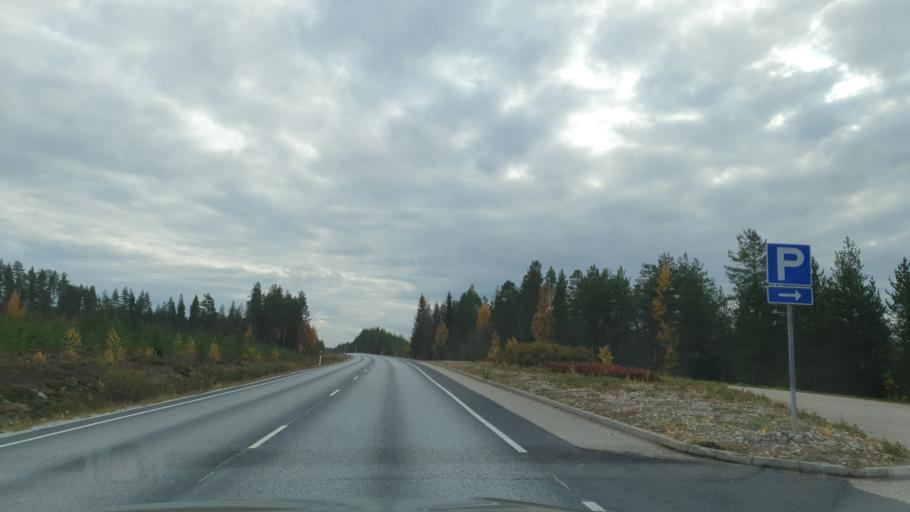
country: FI
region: Northern Ostrobothnia
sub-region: Oulunkaari
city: Pudasjaervi
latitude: 65.4174
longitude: 26.8779
